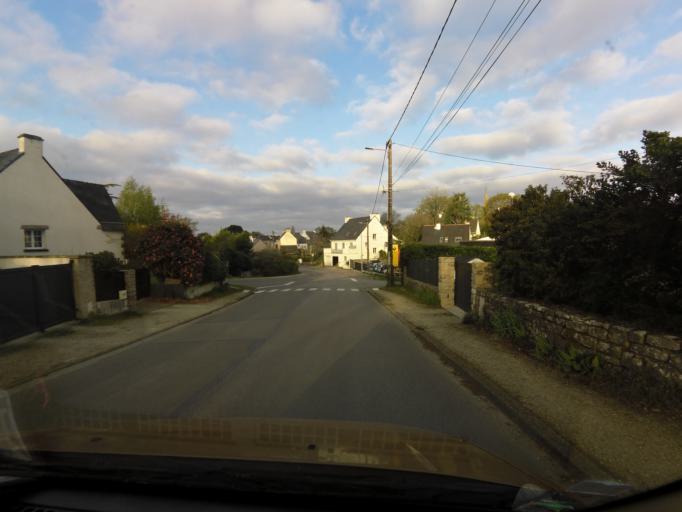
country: FR
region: Brittany
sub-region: Departement du Morbihan
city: Arradon
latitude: 47.6271
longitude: -2.8178
